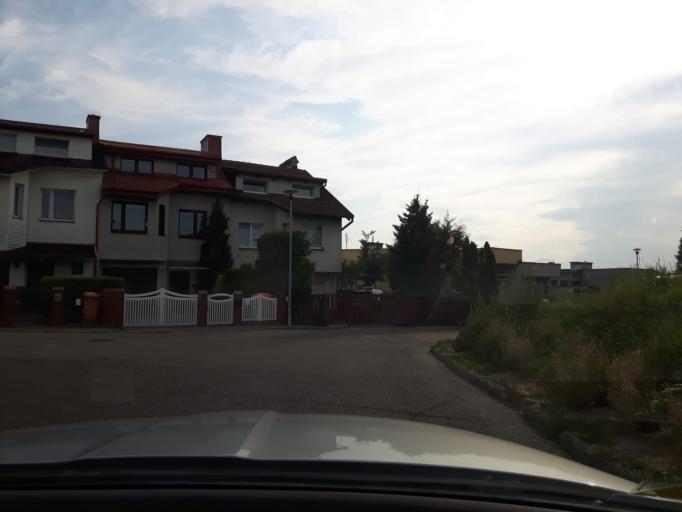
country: PL
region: Pomeranian Voivodeship
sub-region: Gdynia
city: Gdynia
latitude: 54.5024
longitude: 18.5467
